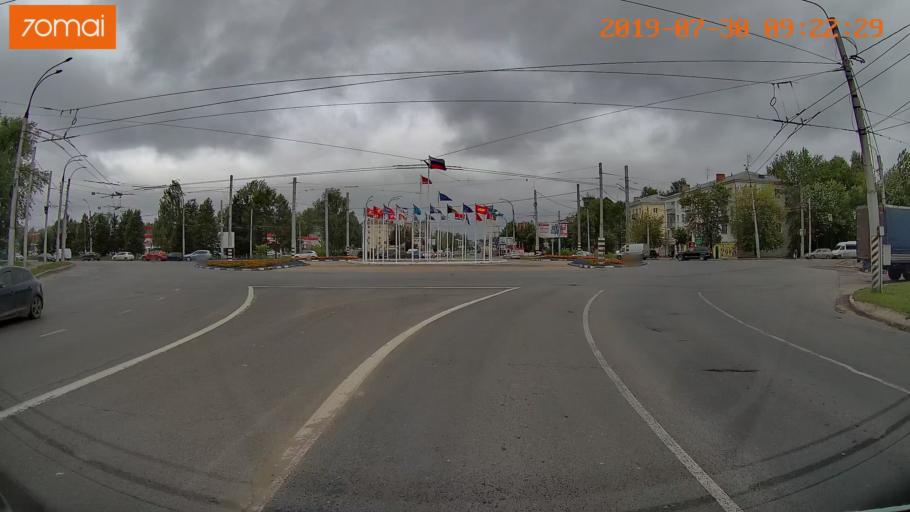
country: RU
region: Ivanovo
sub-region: Gorod Ivanovo
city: Ivanovo
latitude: 56.9637
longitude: 40.9762
